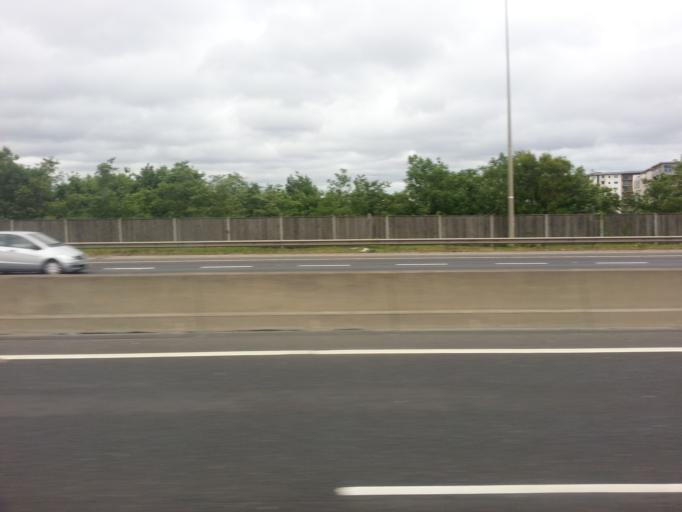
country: IE
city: Cherry Orchard
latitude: 53.3327
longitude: -6.3824
